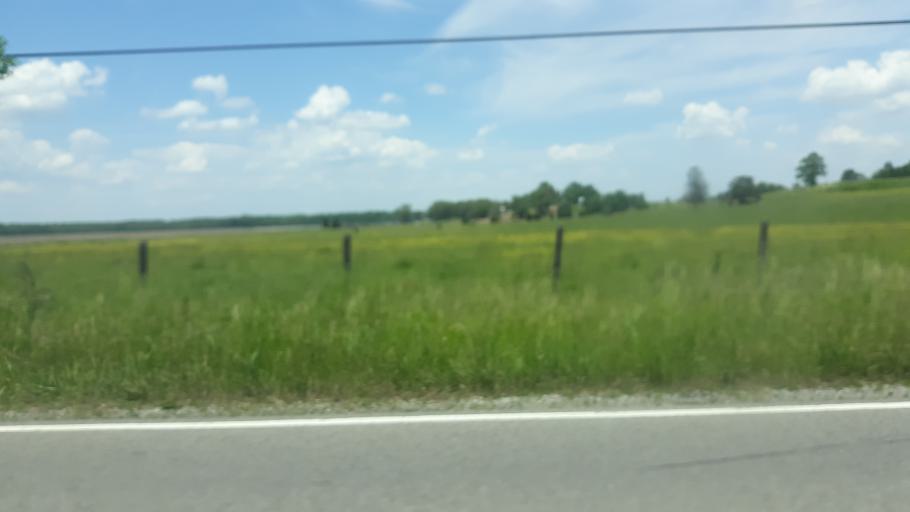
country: US
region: Illinois
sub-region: Saline County
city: Harrisburg
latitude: 37.6365
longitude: -88.5082
